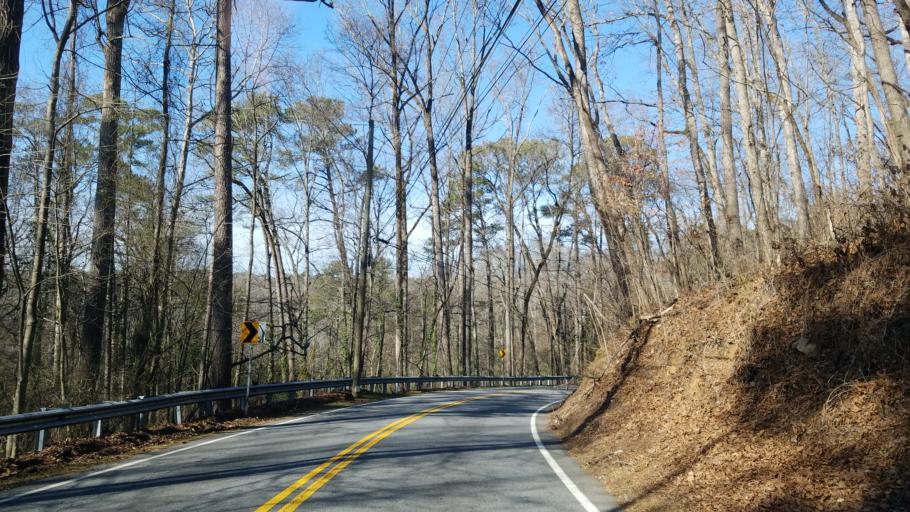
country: US
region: Georgia
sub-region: Fulton County
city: Sandy Springs
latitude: 33.9371
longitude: -84.4091
